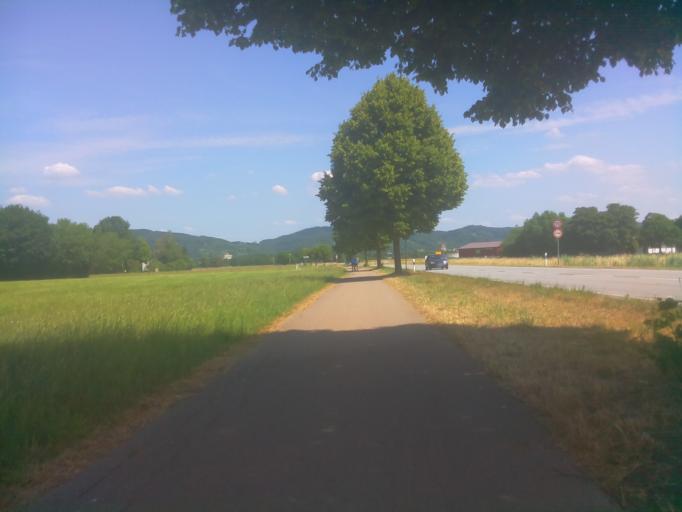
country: DE
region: Baden-Wuerttemberg
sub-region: Karlsruhe Region
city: Hemsbach
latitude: 49.5953
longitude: 8.6142
